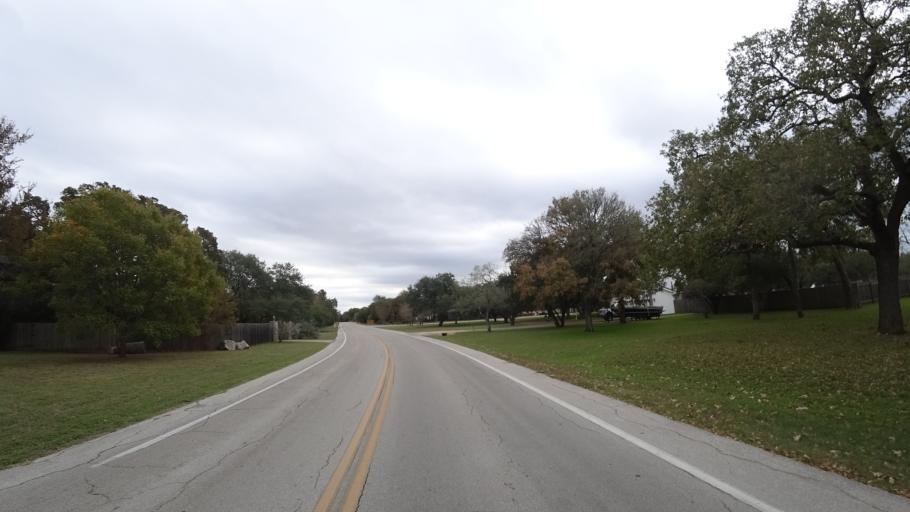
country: US
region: Texas
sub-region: Travis County
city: Shady Hollow
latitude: 30.1585
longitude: -97.8731
